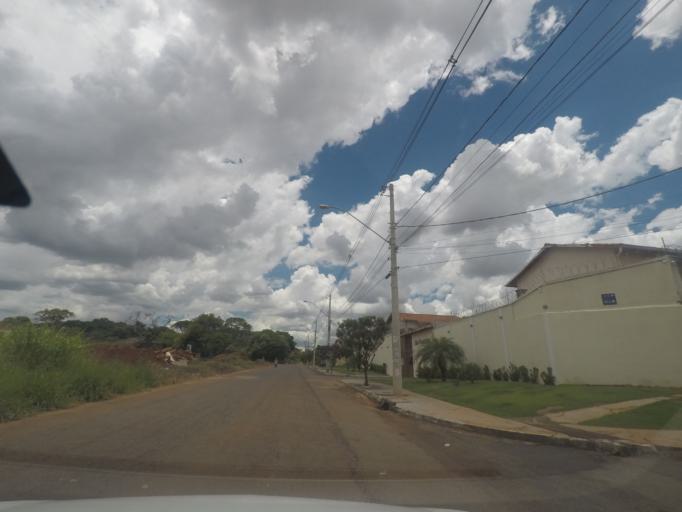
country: BR
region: Goias
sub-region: Goiania
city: Goiania
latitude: -16.7120
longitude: -49.3439
